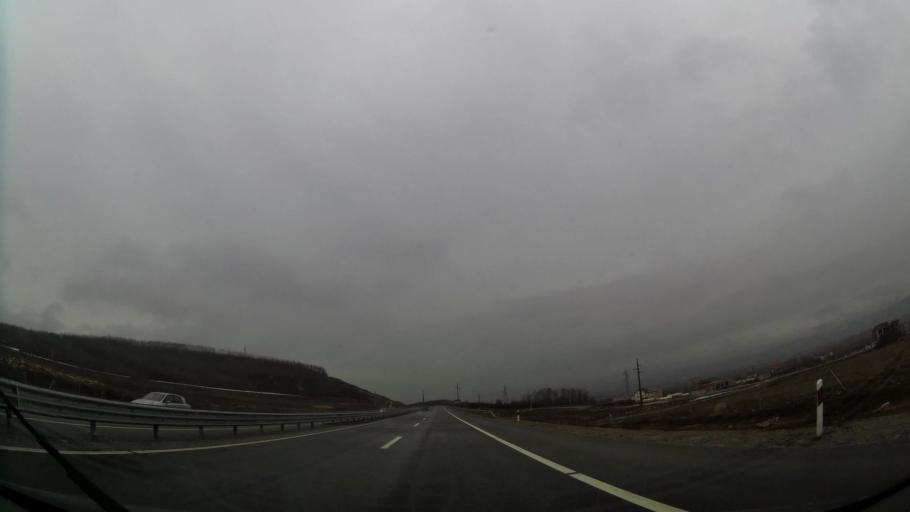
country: XK
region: Ferizaj
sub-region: Komuna e Ferizajt
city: Ferizaj
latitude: 42.3277
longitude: 21.2045
